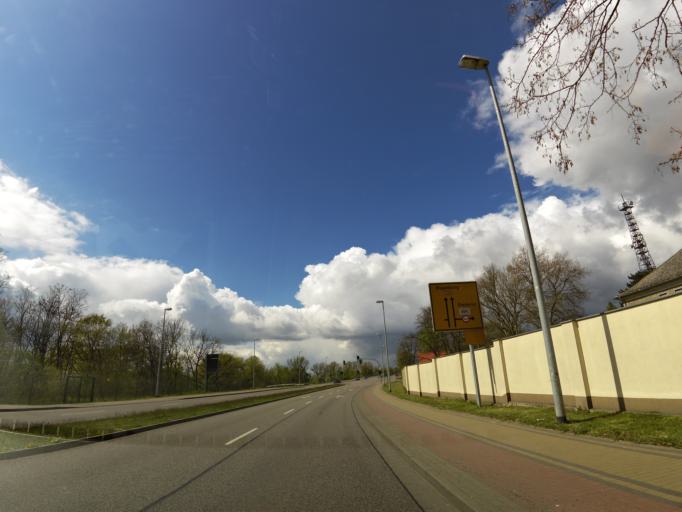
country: DE
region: Saxony-Anhalt
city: Biederitz
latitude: 52.1376
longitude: 11.7327
